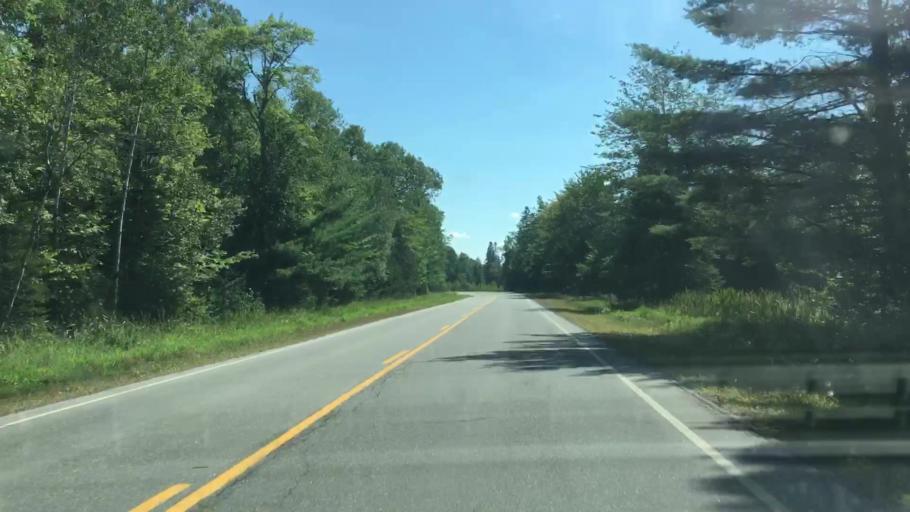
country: US
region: Maine
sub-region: Piscataquis County
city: Milo
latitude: 45.2019
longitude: -68.9072
